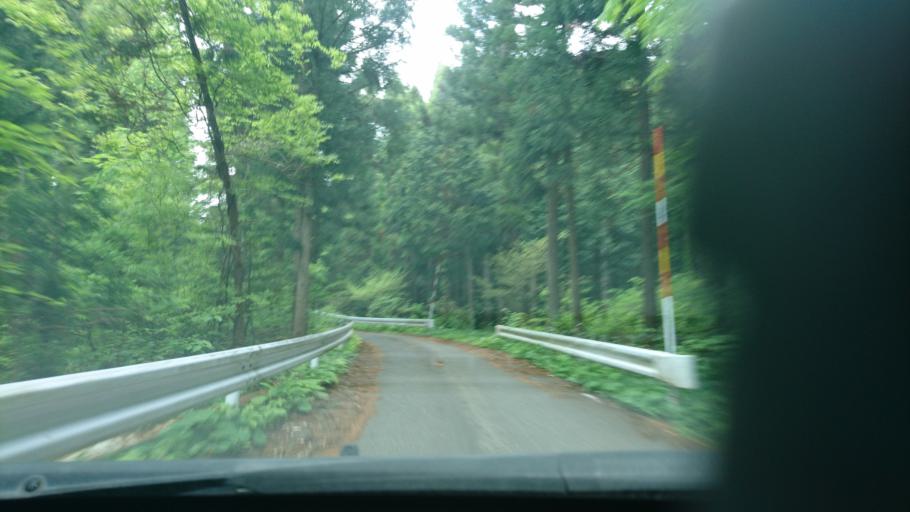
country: JP
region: Iwate
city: Ichinoseki
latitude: 38.9041
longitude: 140.9130
